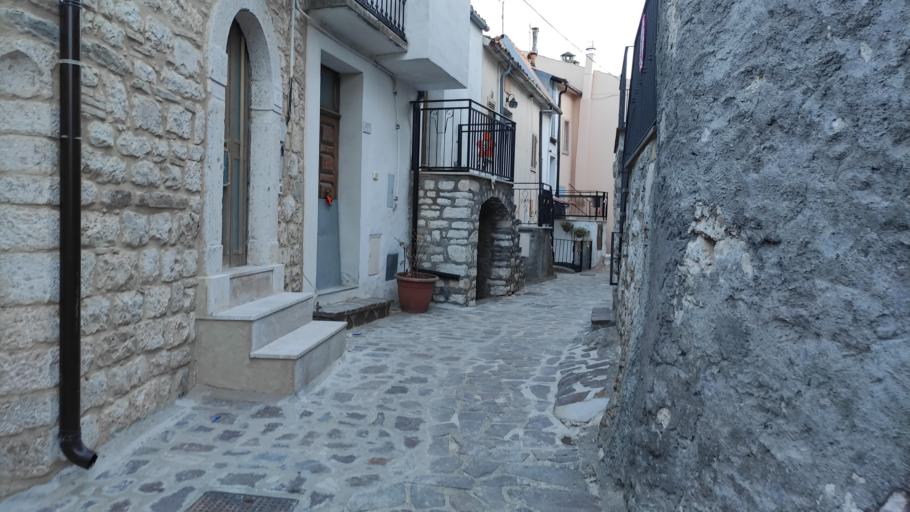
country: IT
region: Abruzzo
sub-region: Provincia di Chieti
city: Fallo
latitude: 41.9381
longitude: 14.3242
